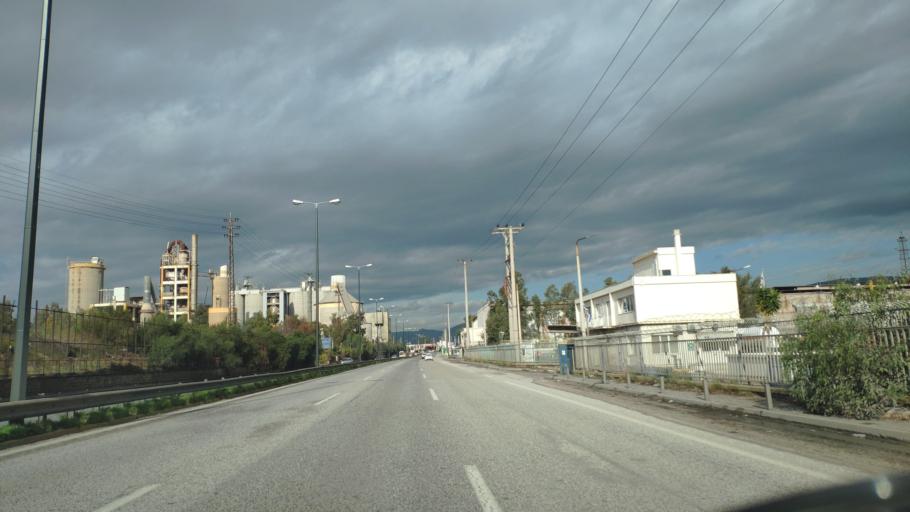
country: GR
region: Attica
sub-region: Nomarchia Athinas
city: Skaramangas
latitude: 38.0320
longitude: 23.5960
